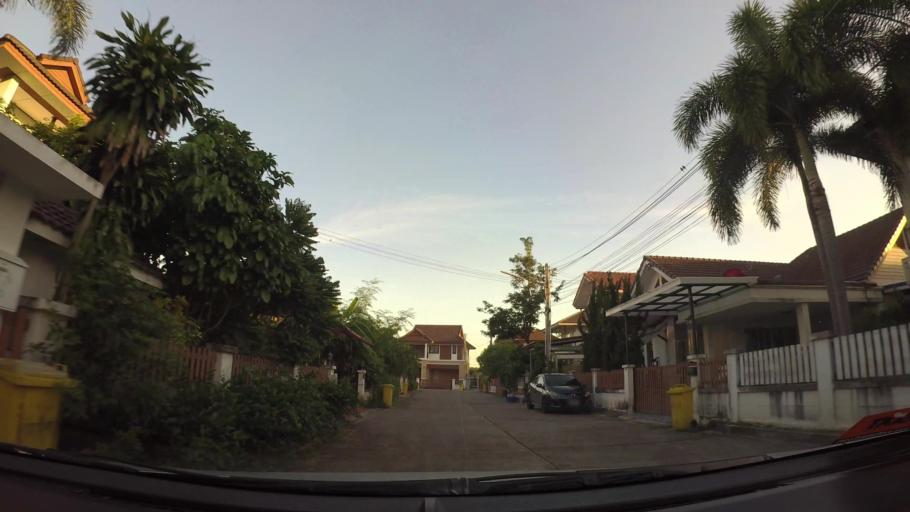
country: TH
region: Chon Buri
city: Si Racha
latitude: 13.1287
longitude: 100.9394
